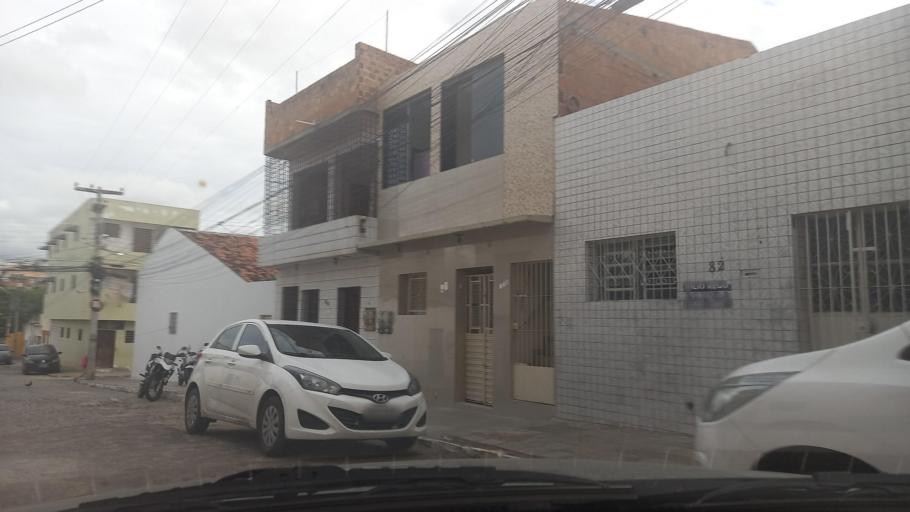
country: BR
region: Pernambuco
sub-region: Caruaru
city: Caruaru
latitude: -8.2918
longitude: -35.9771
